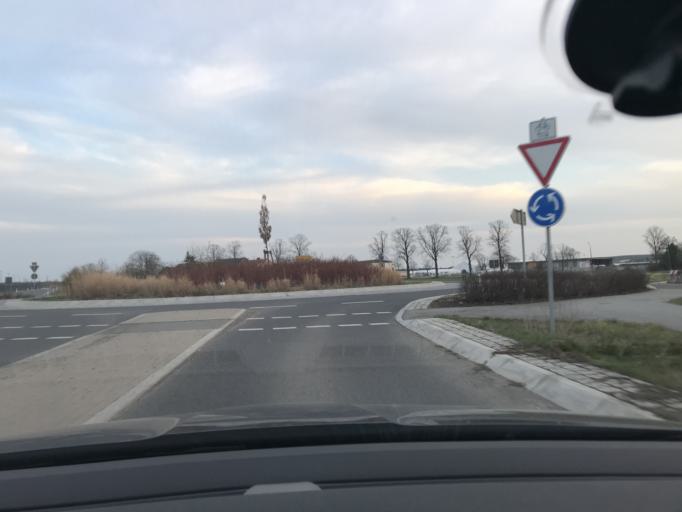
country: DE
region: Brandenburg
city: Schonefeld
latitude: 52.3567
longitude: 13.4801
